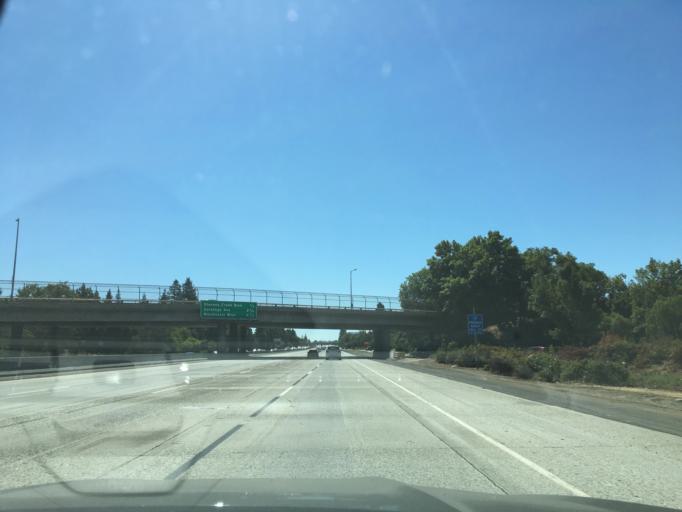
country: US
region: California
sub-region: Santa Clara County
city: Cupertino
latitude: 37.3311
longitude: -122.0155
